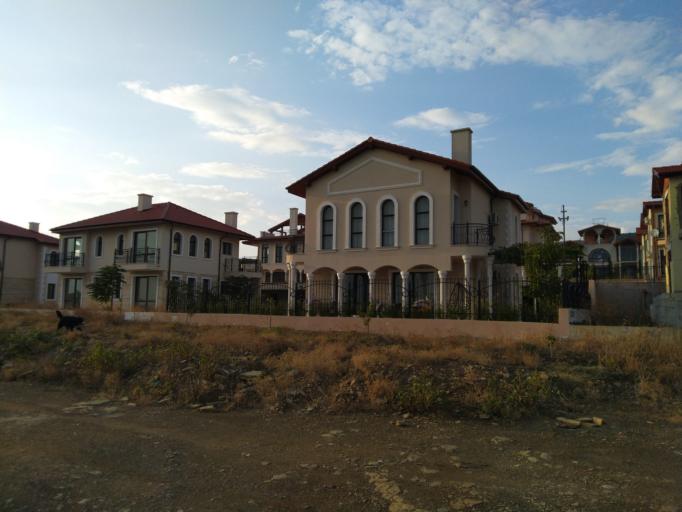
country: BG
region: Burgas
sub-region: Obshtina Nesebur
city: Sveti Vlas
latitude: 42.7144
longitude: 27.7368
